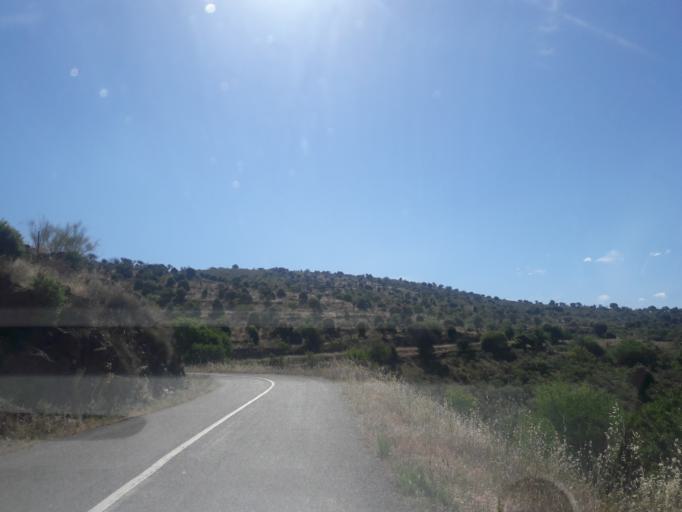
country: ES
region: Castille and Leon
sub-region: Provincia de Salamanca
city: Saucelle
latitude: 41.0202
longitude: -6.7527
